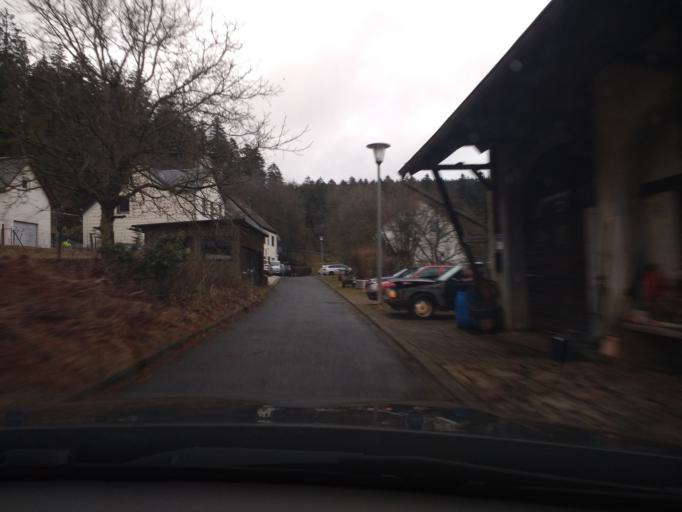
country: DE
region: Rheinland-Pfalz
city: Borfink
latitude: 49.6772
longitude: 7.0491
